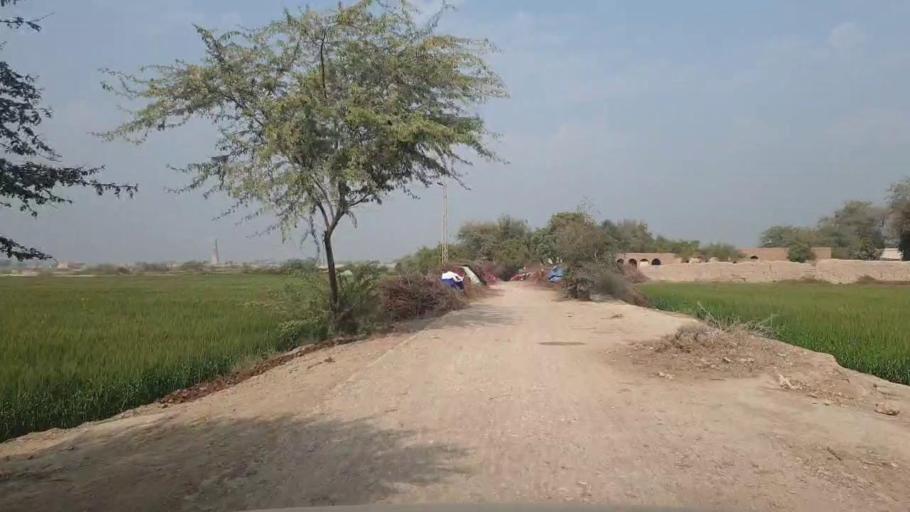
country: PK
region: Sindh
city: Hala
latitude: 25.7847
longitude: 68.4295
